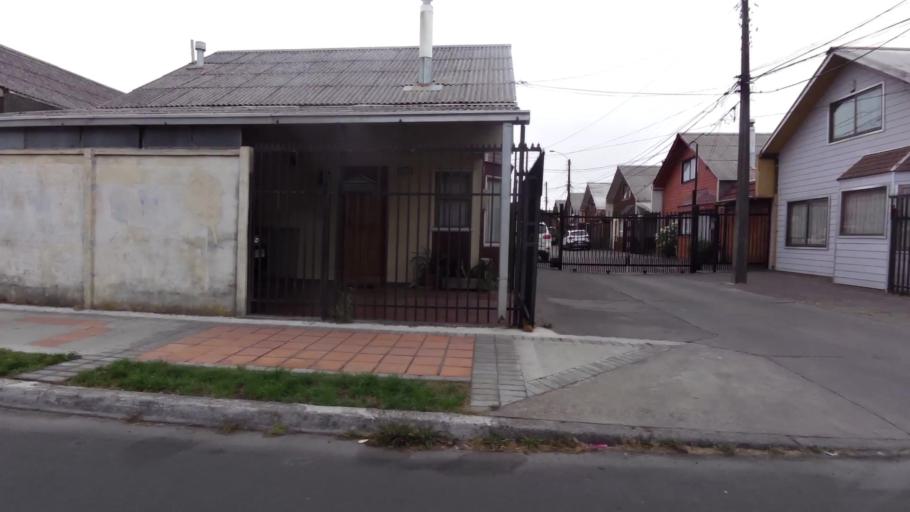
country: CL
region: Biobio
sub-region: Provincia de Concepcion
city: Concepcion
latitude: -36.7913
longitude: -73.0821
